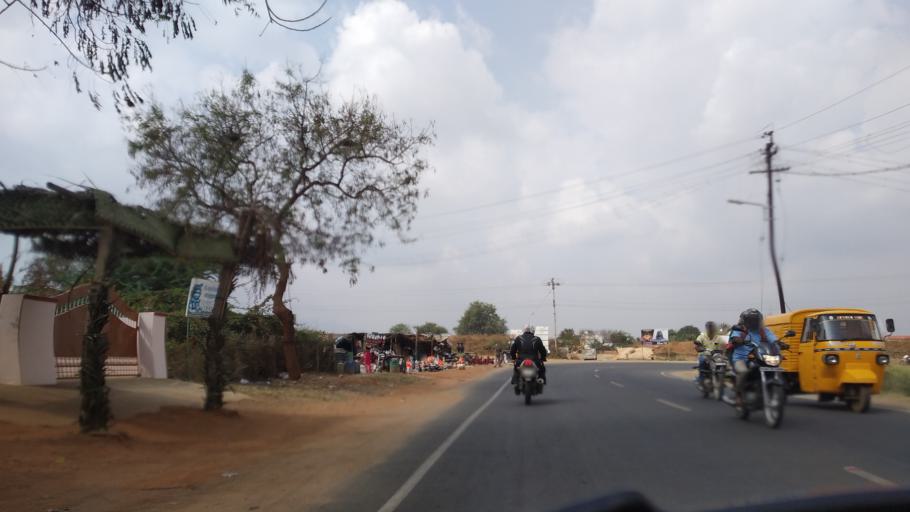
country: IN
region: Tamil Nadu
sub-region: Coimbatore
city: Perur
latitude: 10.9546
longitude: 76.9269
